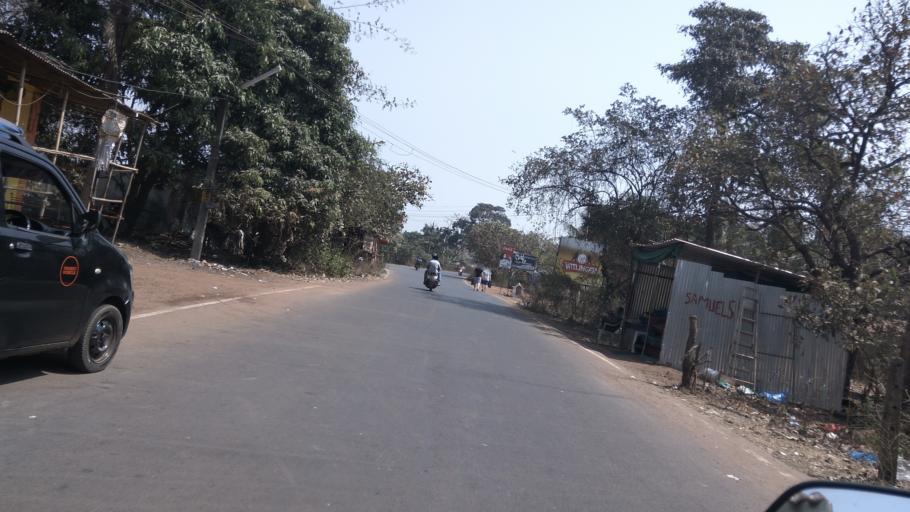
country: IN
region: Goa
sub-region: North Goa
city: Vagator
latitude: 15.5974
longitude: 73.7481
